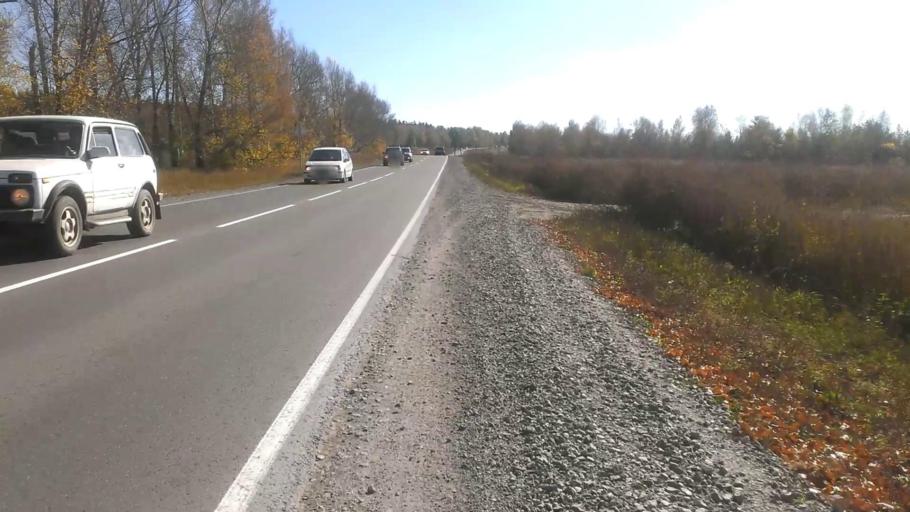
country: RU
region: Altai Krai
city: Sannikovo
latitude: 53.3067
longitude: 83.9683
